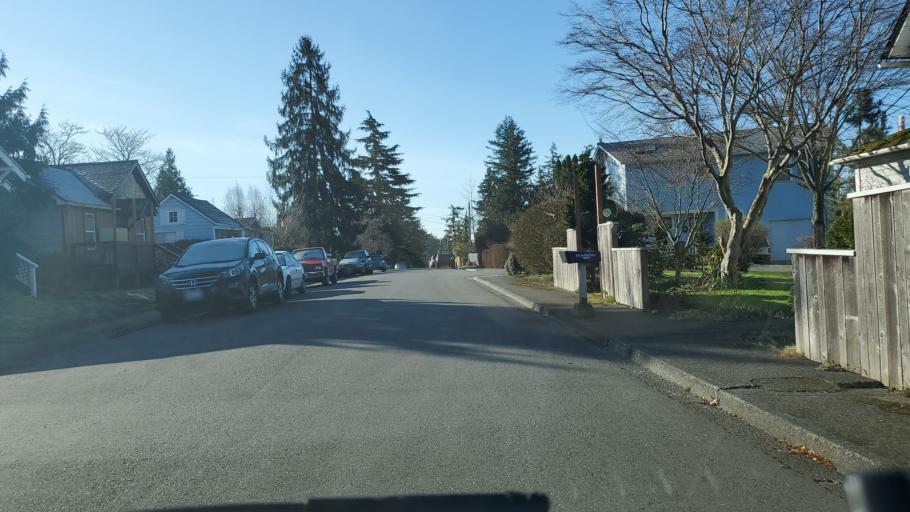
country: US
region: Washington
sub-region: Skagit County
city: Mount Vernon
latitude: 48.4200
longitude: -122.3298
